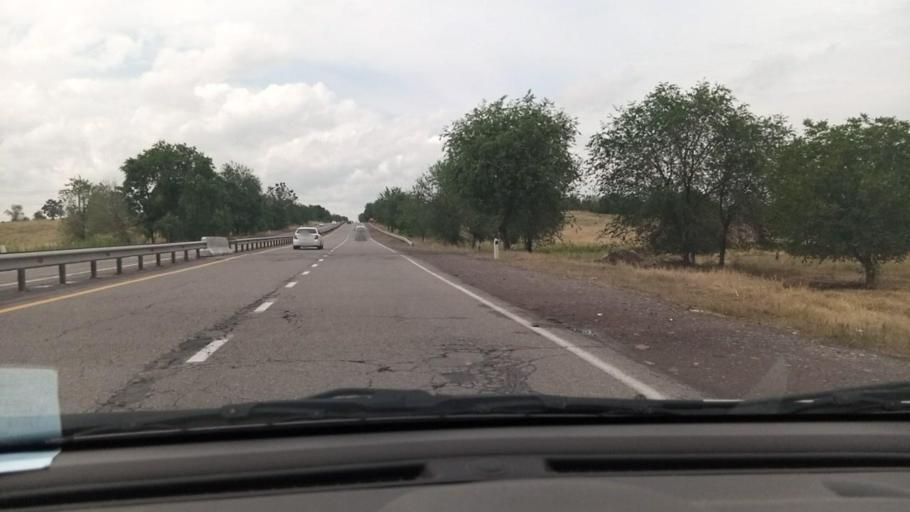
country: UZ
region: Toshkent
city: Ohangaron
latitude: 41.0037
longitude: 69.5244
